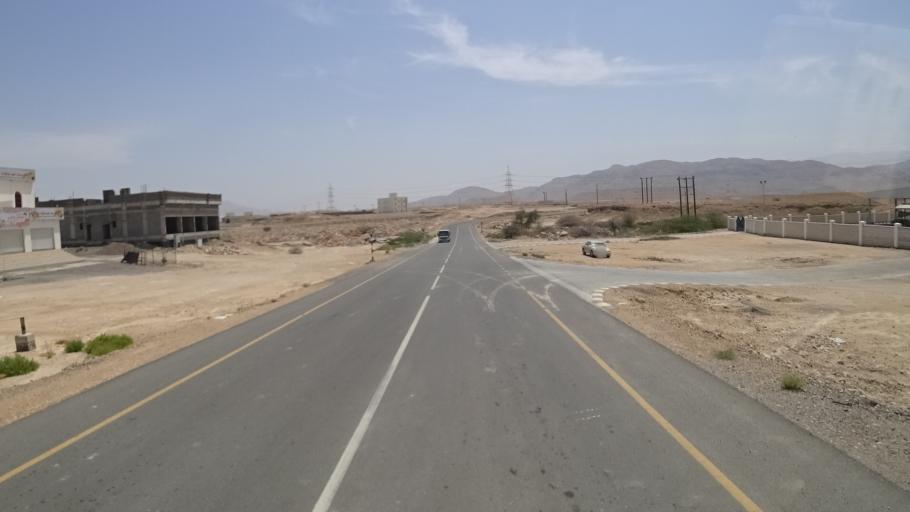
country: OM
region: Ash Sharqiyah
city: Sur
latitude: 22.5923
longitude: 59.4581
